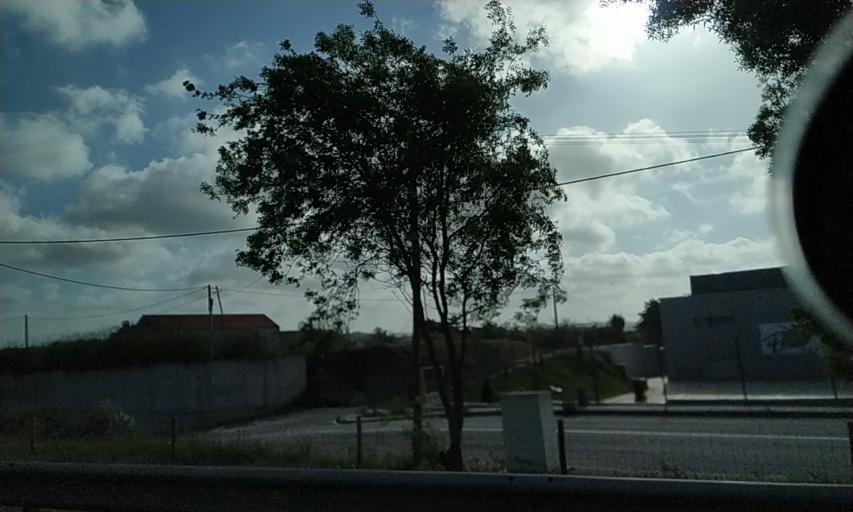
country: PT
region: Leiria
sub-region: Obidos
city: Obidos
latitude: 39.3336
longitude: -9.1743
